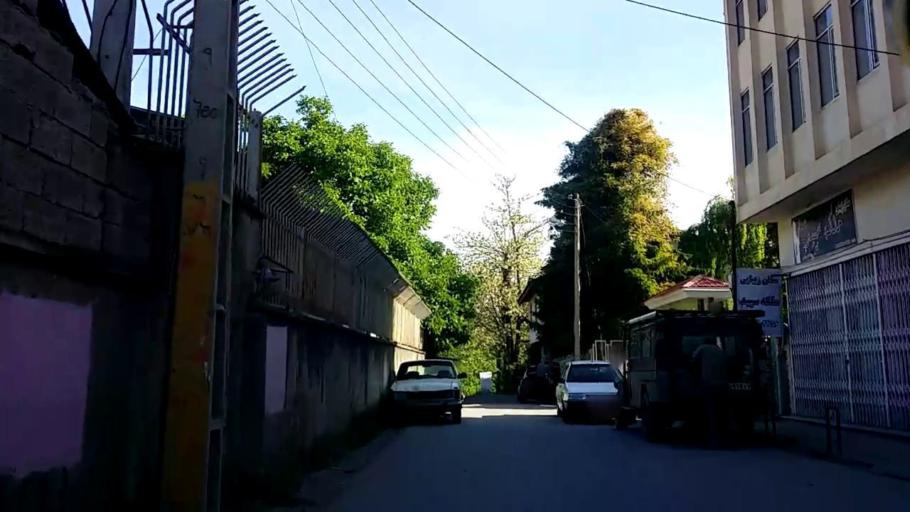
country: IR
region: Mazandaran
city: `Abbasabad
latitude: 36.5072
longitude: 51.1606
